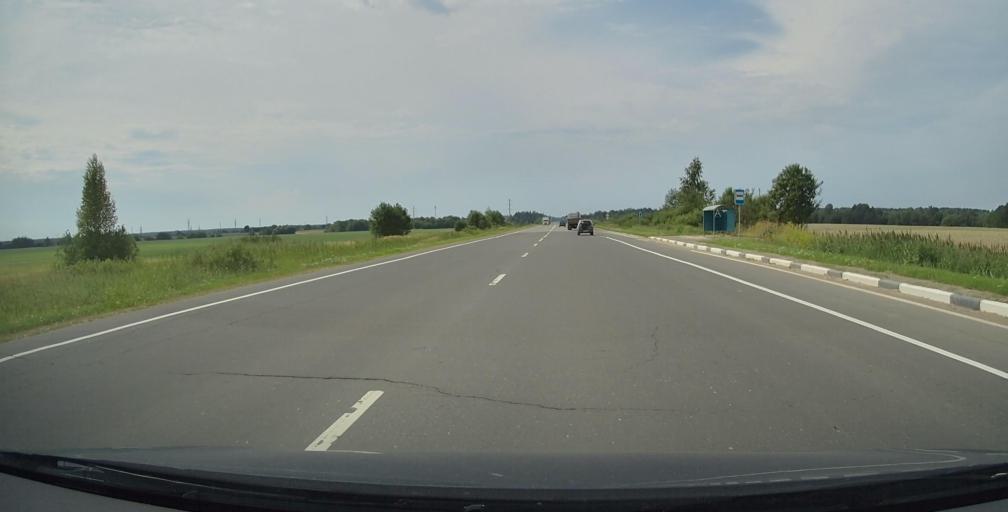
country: RU
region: Jaroslavl
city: Pesochnoye
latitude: 57.9841
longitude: 39.1376
